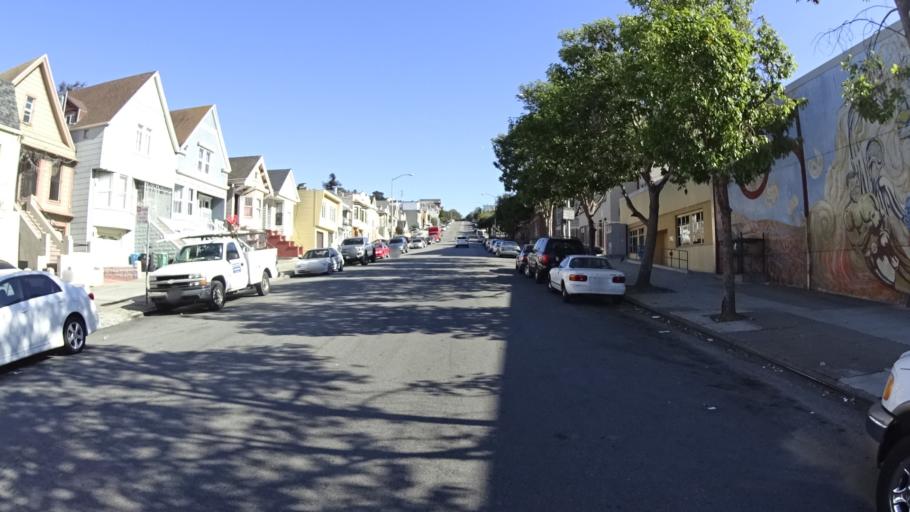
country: US
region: California
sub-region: San Francisco County
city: San Francisco
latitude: 37.7351
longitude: -122.3896
